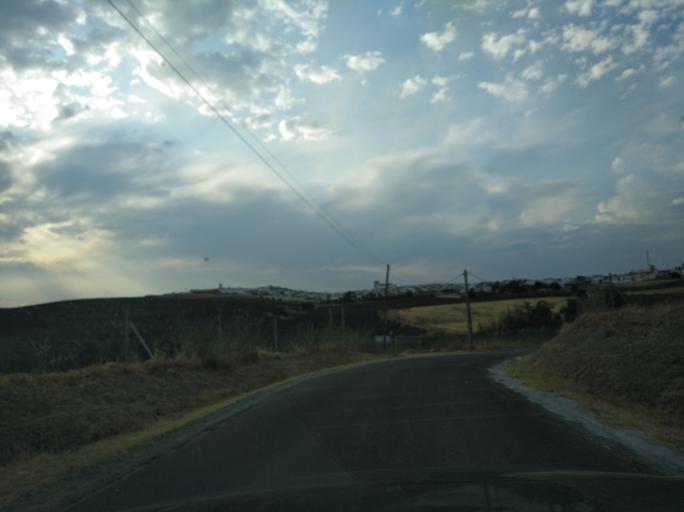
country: PT
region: Portalegre
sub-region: Campo Maior
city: Campo Maior
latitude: 39.0050
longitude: -7.0602
